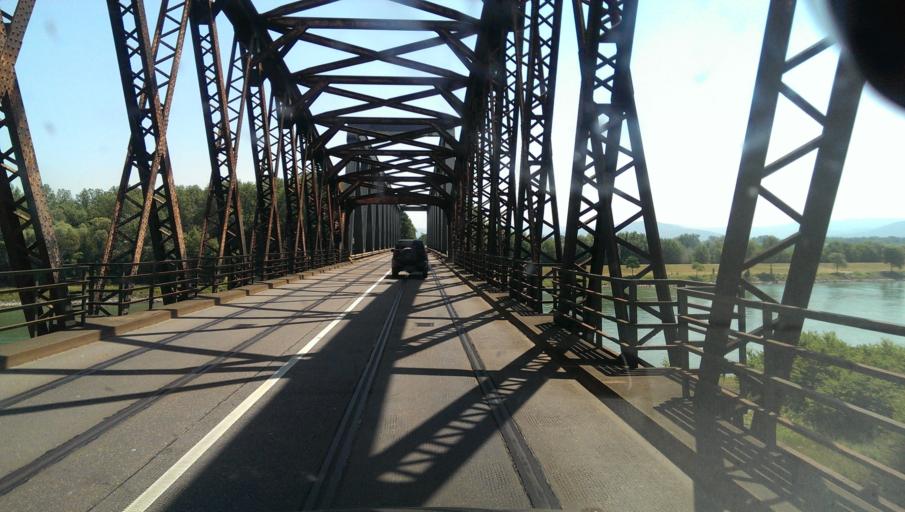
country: DE
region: Baden-Wuerttemberg
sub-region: Karlsruhe Region
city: Iffezheim
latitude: 48.8476
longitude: 8.1144
